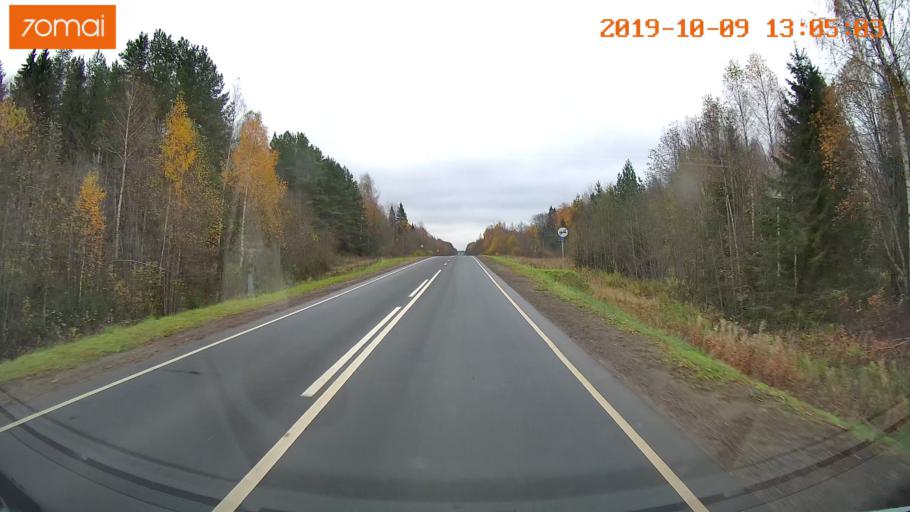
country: RU
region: Jaroslavl
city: Lyubim
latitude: 58.3578
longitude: 40.5710
